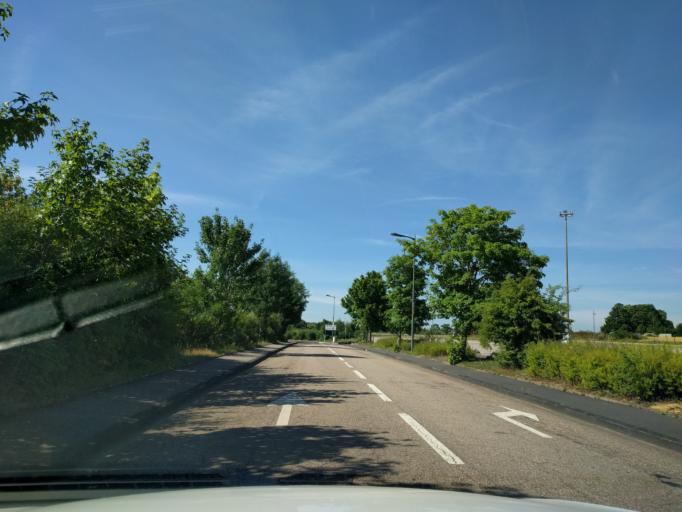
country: FR
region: Lorraine
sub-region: Departement de la Moselle
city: Peltre
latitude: 49.0897
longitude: 6.2326
